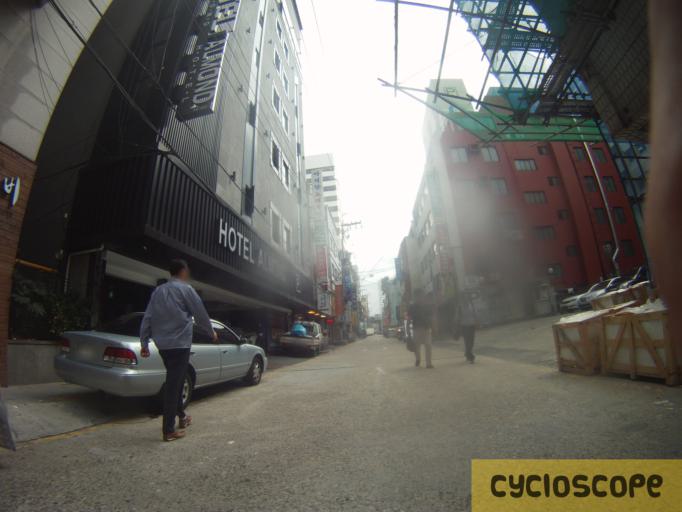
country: KR
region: Busan
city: Busan
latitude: 35.1116
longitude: 129.0394
